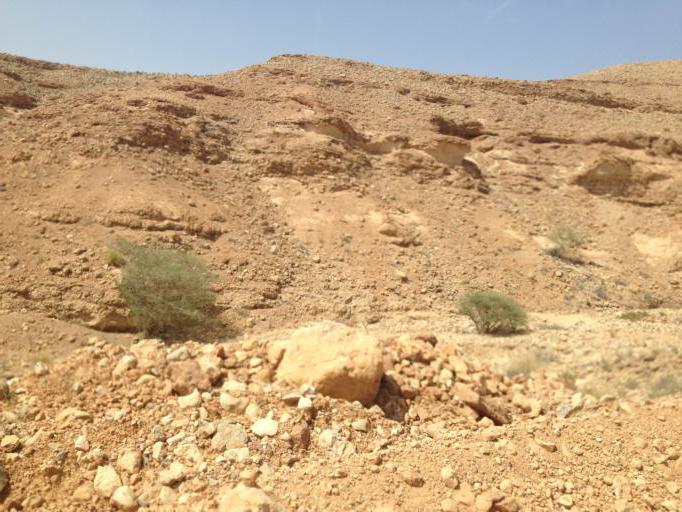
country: OM
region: Ash Sharqiyah
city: Ibra'
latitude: 23.0742
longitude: 58.8846
